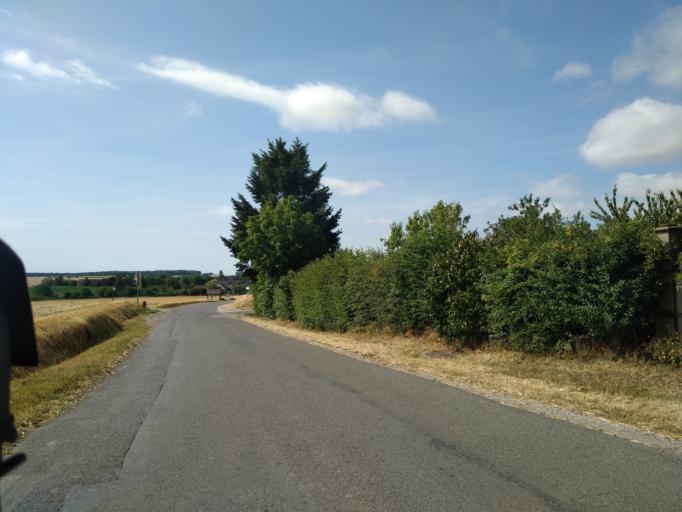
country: FR
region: Auvergne
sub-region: Departement de l'Allier
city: Saint-Pourcain-sur-Sioule
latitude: 46.2719
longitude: 3.2225
